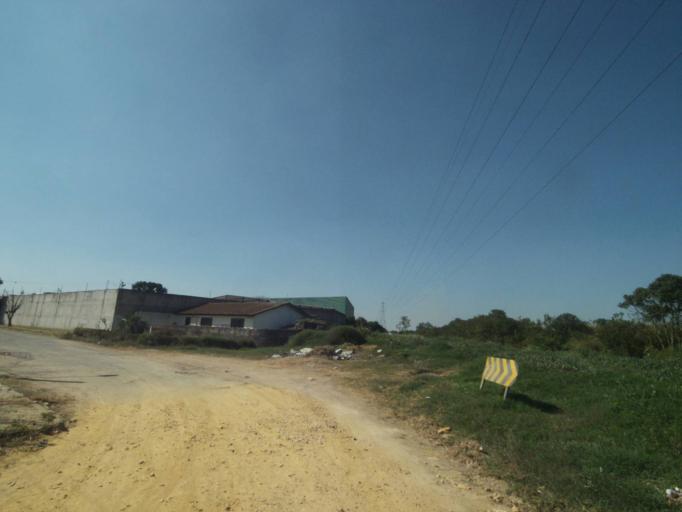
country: BR
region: Parana
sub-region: Sao Jose Dos Pinhais
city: Sao Jose dos Pinhais
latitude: -25.5151
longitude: -49.2199
